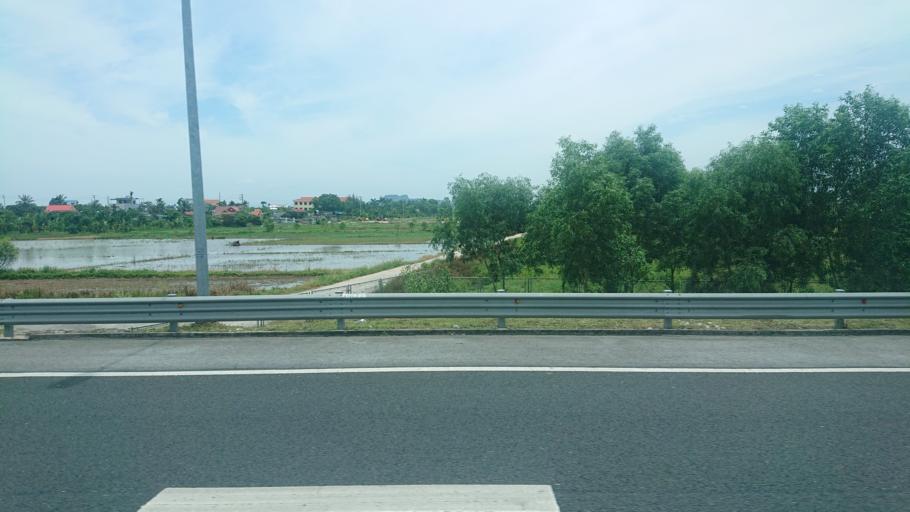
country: VN
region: Hai Phong
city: An Lao
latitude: 20.7952
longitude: 106.5454
